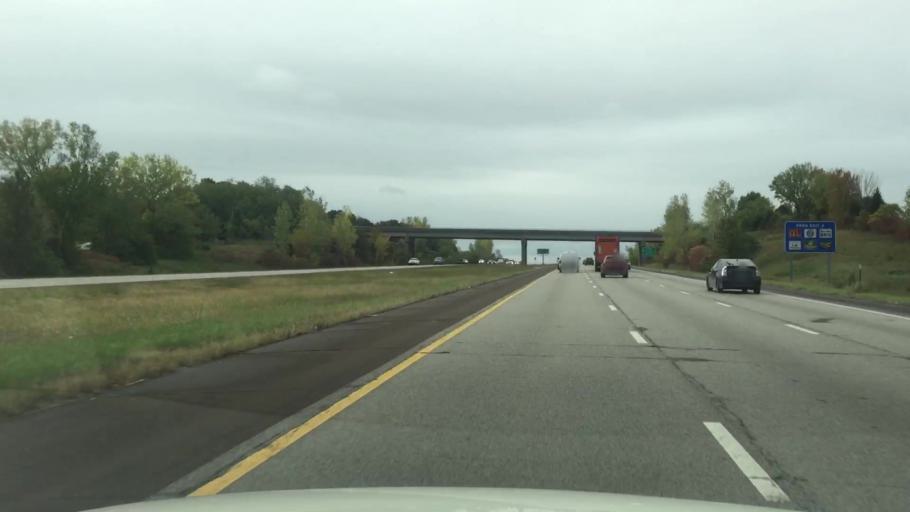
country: US
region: Kansas
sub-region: Johnson County
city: Lenexa
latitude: 38.9879
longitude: -94.7763
